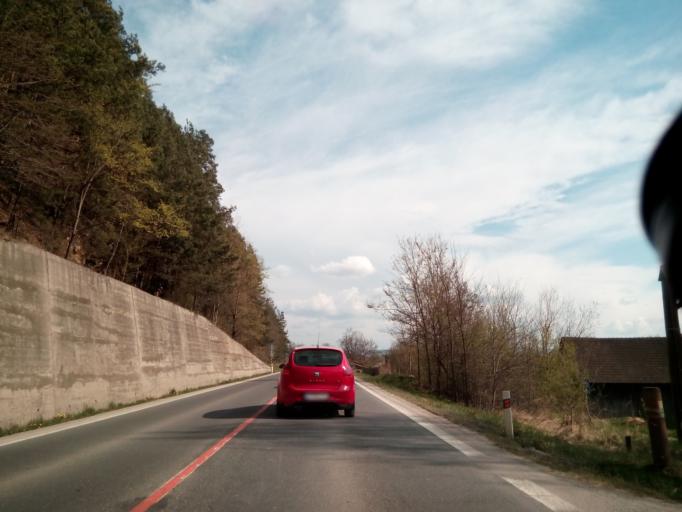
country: SK
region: Presovsky
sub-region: Okres Presov
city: Levoca
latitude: 49.0056
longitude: 20.6373
